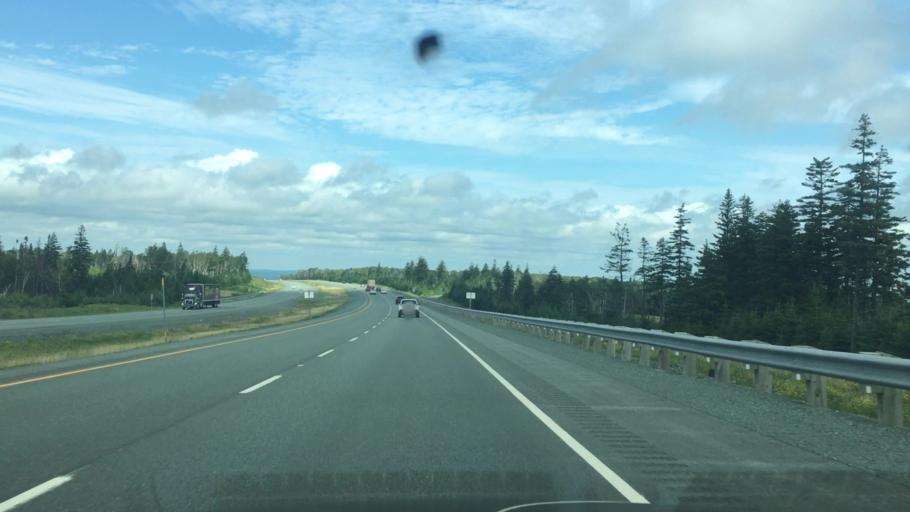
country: CA
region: Nova Scotia
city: Oxford
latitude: 45.5761
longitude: -63.7133
